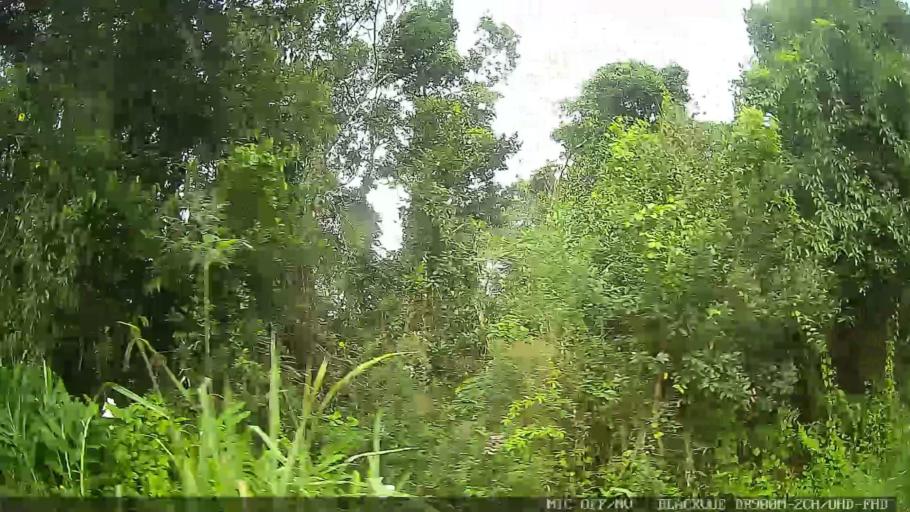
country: BR
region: Sao Paulo
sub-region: Peruibe
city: Peruibe
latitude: -24.2255
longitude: -46.9233
